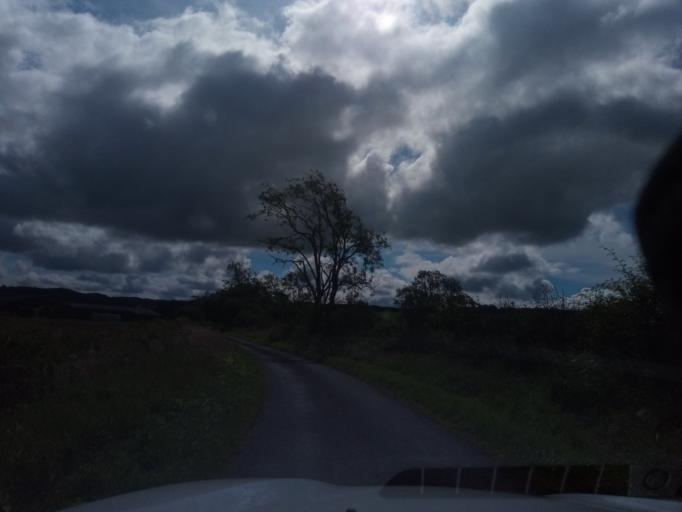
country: GB
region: Scotland
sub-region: The Scottish Borders
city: Saint Boswells
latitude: 55.6038
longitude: -2.6070
